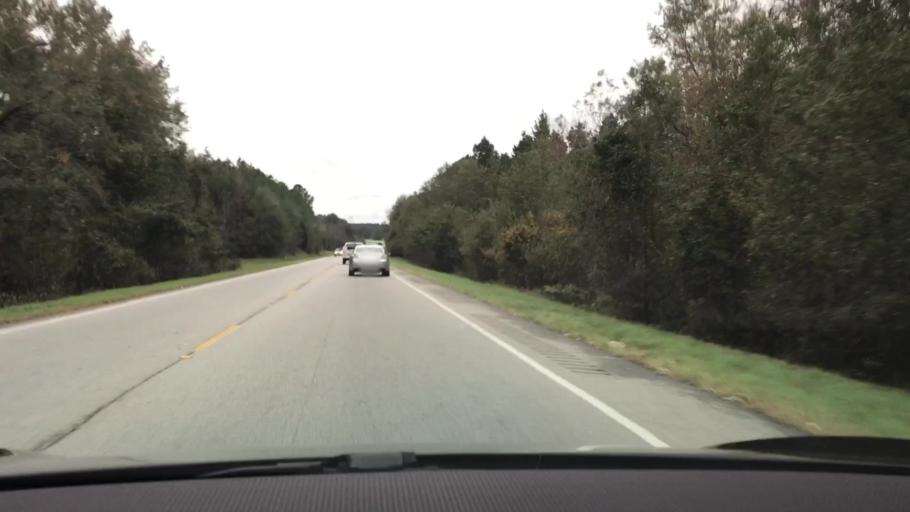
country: US
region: Georgia
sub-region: Jefferson County
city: Wadley
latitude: 32.9013
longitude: -82.4001
